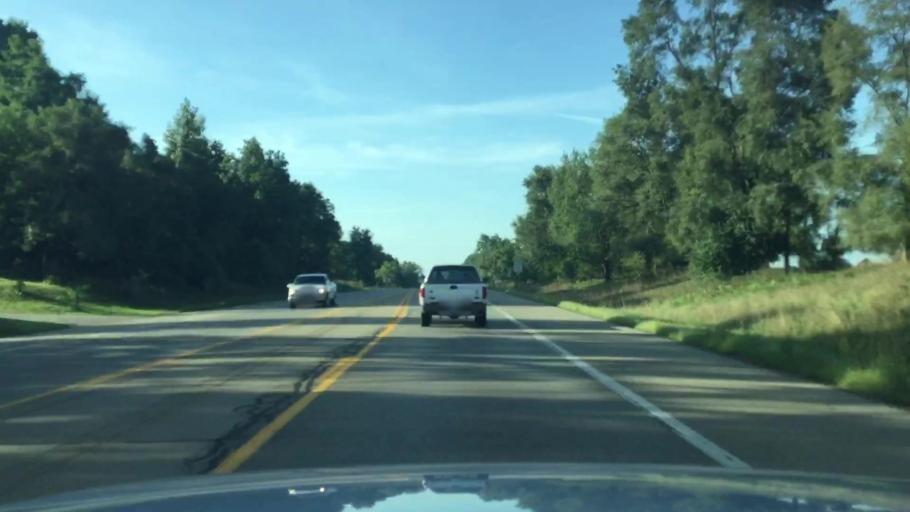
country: US
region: Michigan
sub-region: Jackson County
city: Vandercook Lake
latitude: 42.1704
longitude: -84.3647
